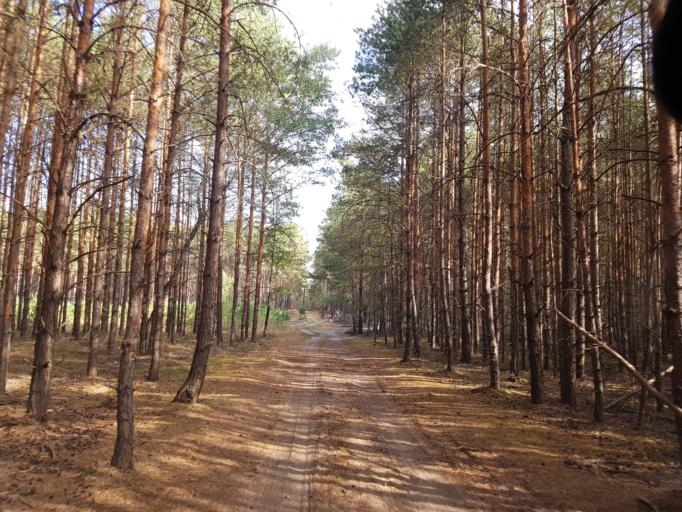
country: DE
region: Brandenburg
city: Finsterwalde
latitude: 51.5914
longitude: 13.7579
